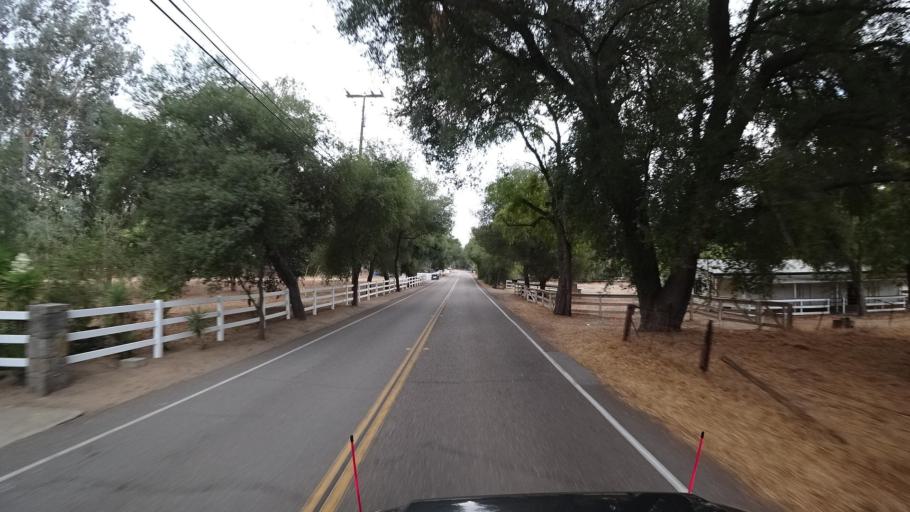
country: US
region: California
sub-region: San Diego County
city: Ramona
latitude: 32.9706
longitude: -116.9143
